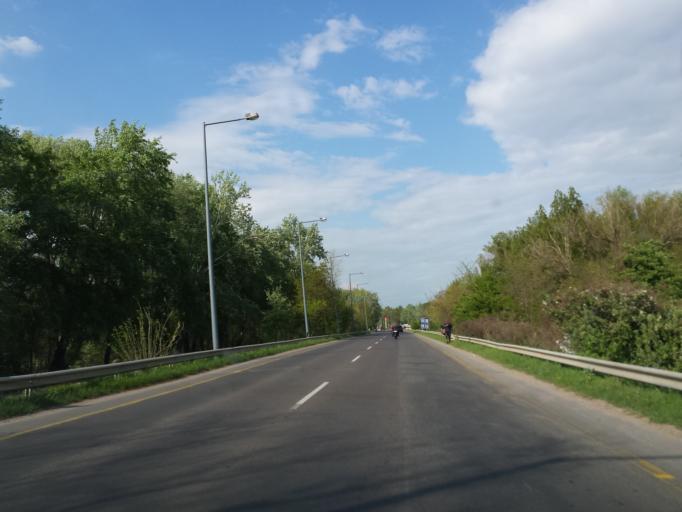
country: HU
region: Csongrad
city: Kiszombor
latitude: 46.2032
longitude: 20.4538
